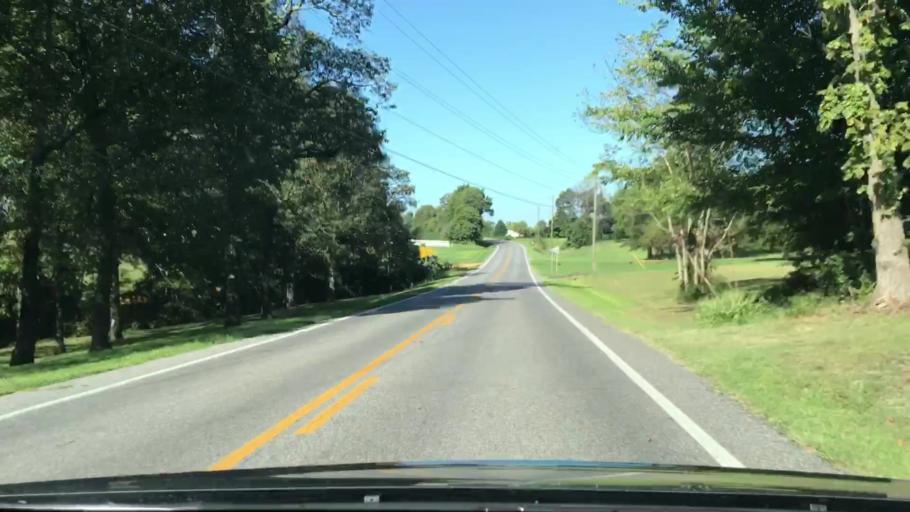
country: US
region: Kentucky
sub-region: Graves County
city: Mayfield
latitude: 36.7658
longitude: -88.5719
